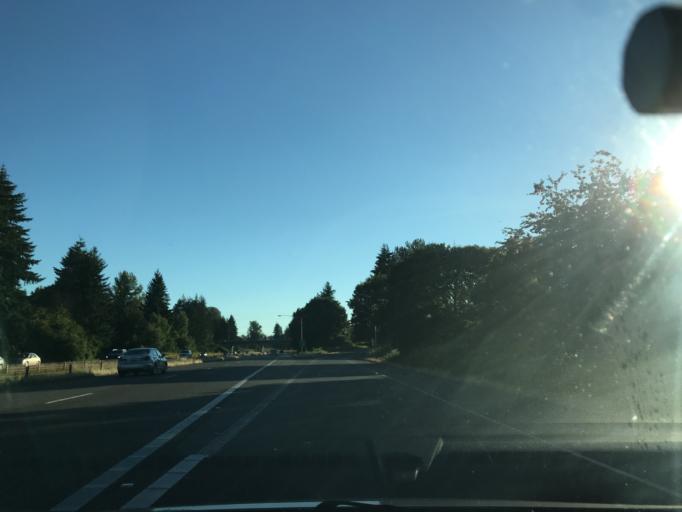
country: US
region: Washington
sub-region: Pierce County
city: Sumner
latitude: 47.1939
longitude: -122.2252
